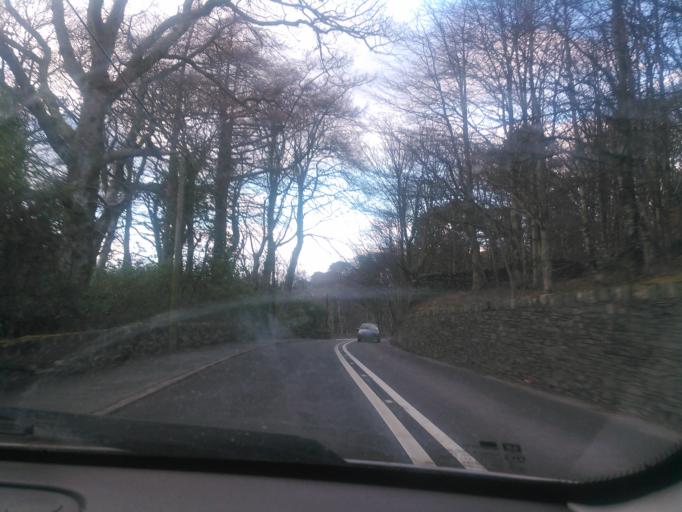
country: GB
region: Wales
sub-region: Gwynedd
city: Bethesda
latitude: 53.1686
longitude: -4.0559
